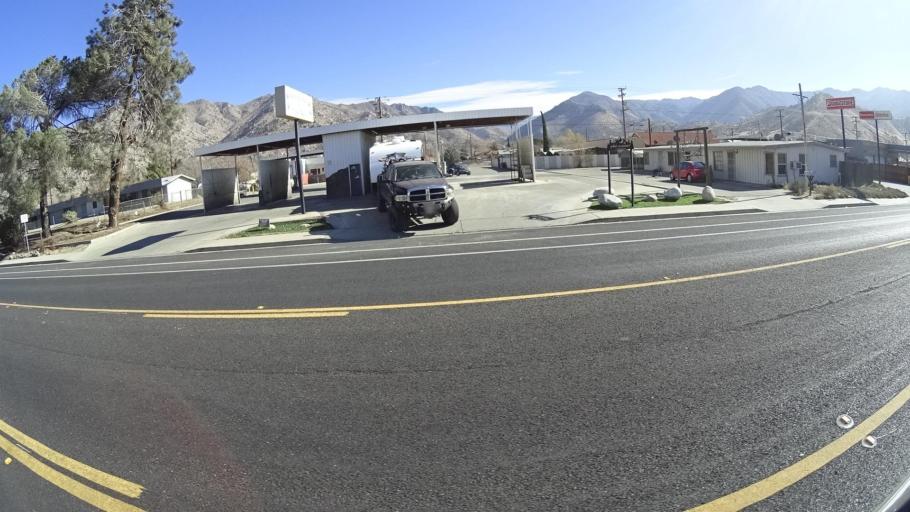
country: US
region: California
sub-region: Kern County
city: Lake Isabella
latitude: 35.6135
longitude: -118.4807
